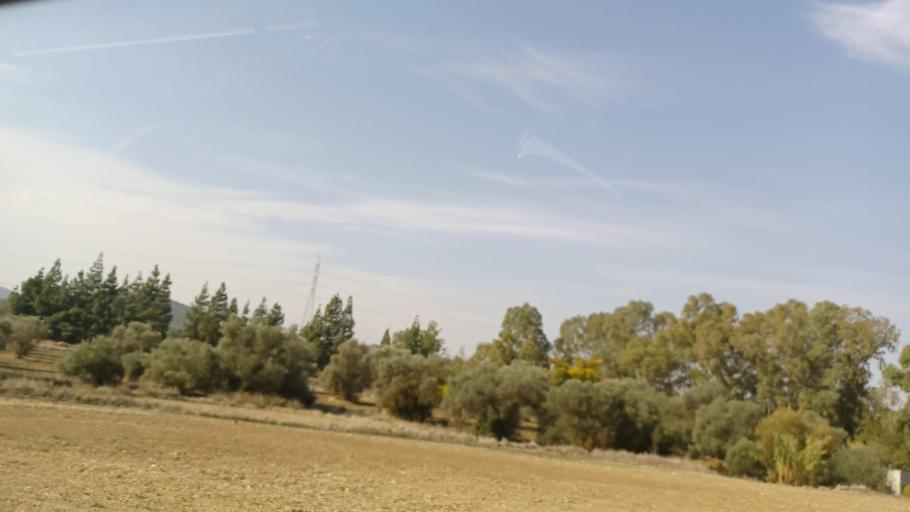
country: CY
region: Larnaka
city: Mosfiloti
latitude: 34.9671
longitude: 33.4138
